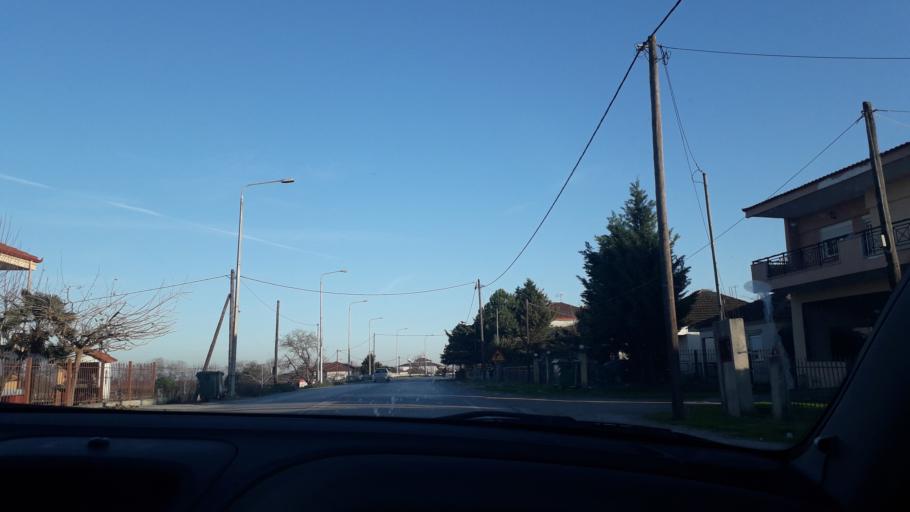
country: GR
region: Central Macedonia
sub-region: Nomos Imathias
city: Alexandreia
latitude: 40.5972
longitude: 22.4606
